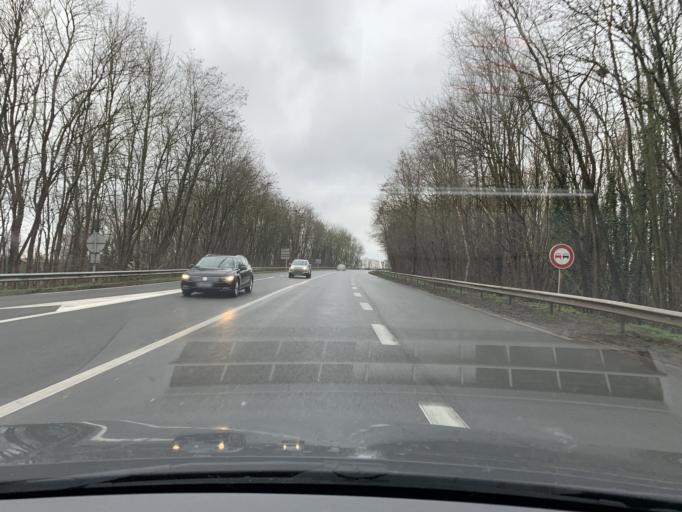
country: FR
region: Nord-Pas-de-Calais
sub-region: Departement du Nord
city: Dechy
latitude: 50.3564
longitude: 3.1221
